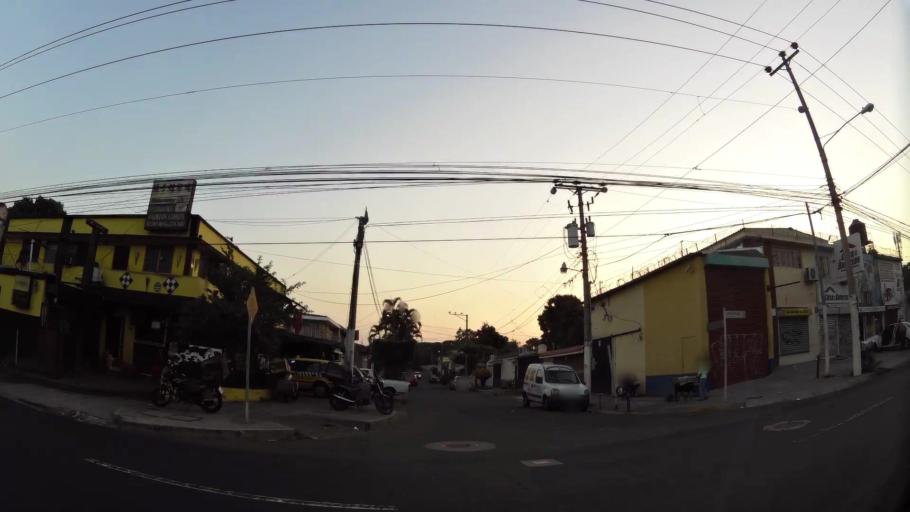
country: SV
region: San Salvador
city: Mejicanos
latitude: 13.7176
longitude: -89.2212
